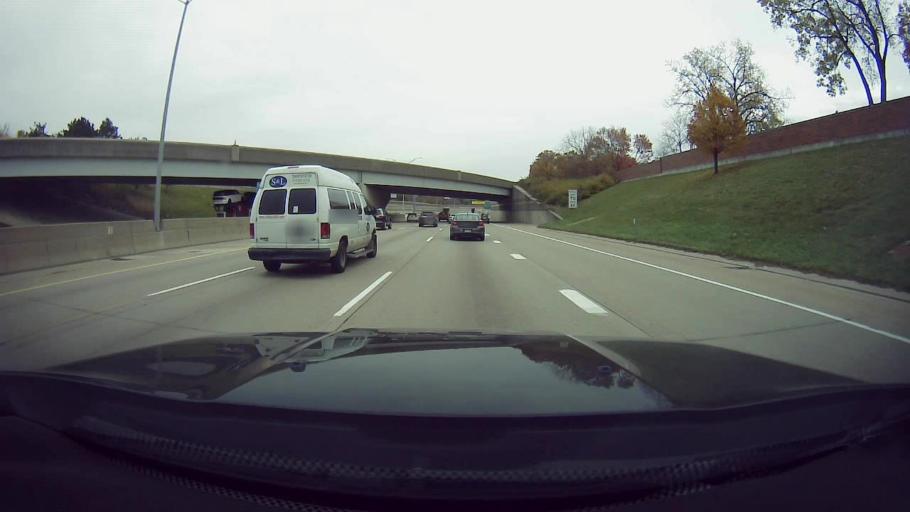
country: US
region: Michigan
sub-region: Oakland County
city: Lathrup Village
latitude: 42.4862
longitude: -83.2523
